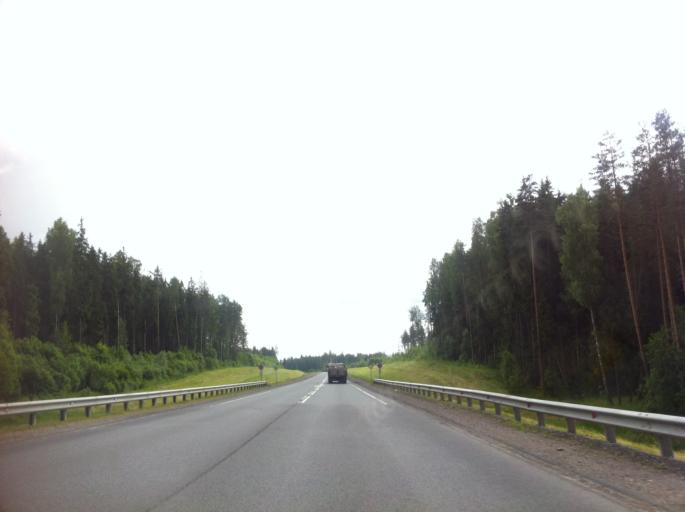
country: RU
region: Leningrad
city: Luga
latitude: 58.7697
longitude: 29.8813
